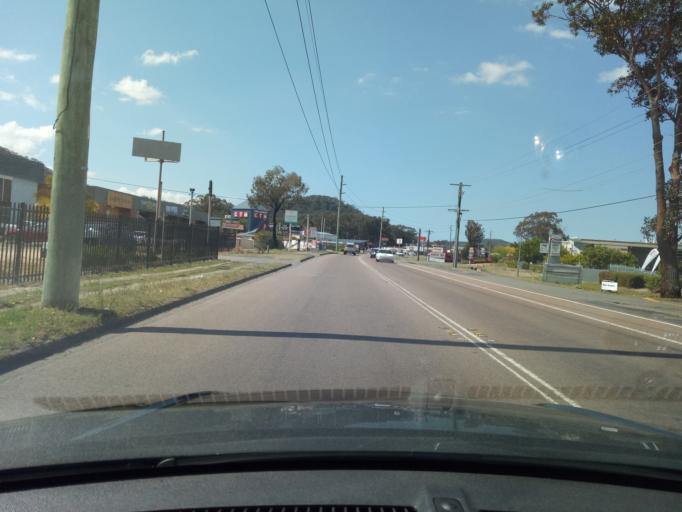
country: AU
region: New South Wales
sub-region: Gosford Shire
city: Gosford
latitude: -33.4179
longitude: 151.3218
